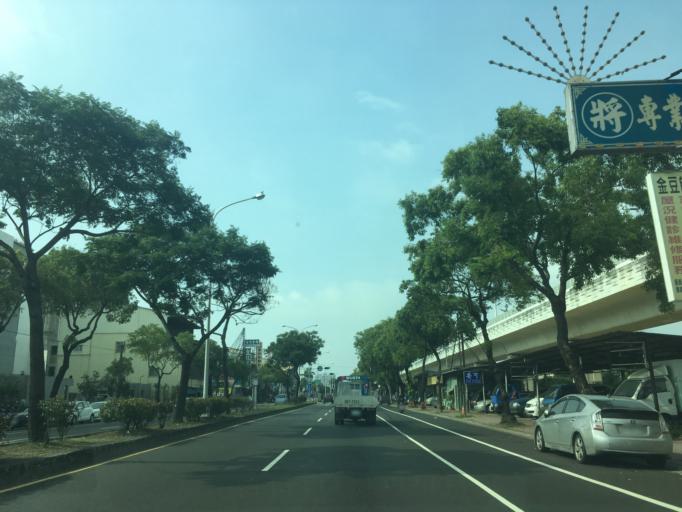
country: TW
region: Taiwan
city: Fengyuan
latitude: 24.2246
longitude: 120.7074
